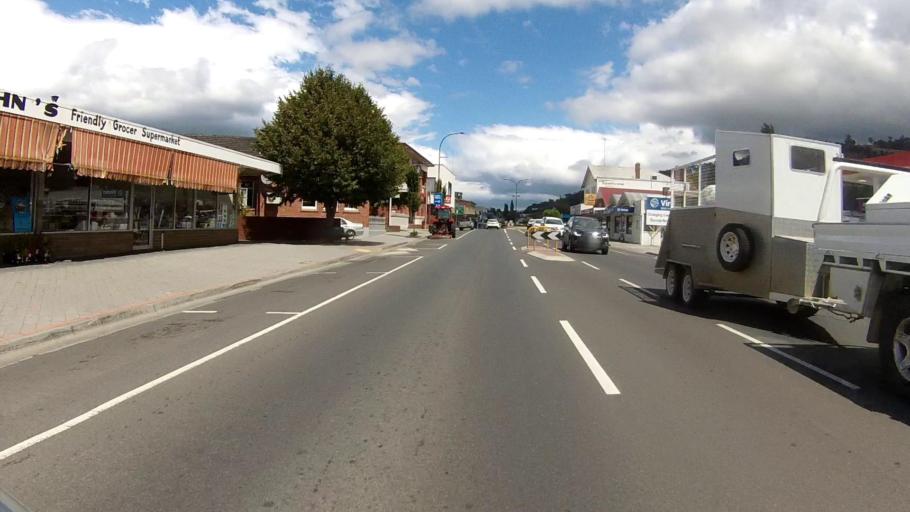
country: AU
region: Tasmania
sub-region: Huon Valley
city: Huonville
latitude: -43.0298
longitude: 147.0490
